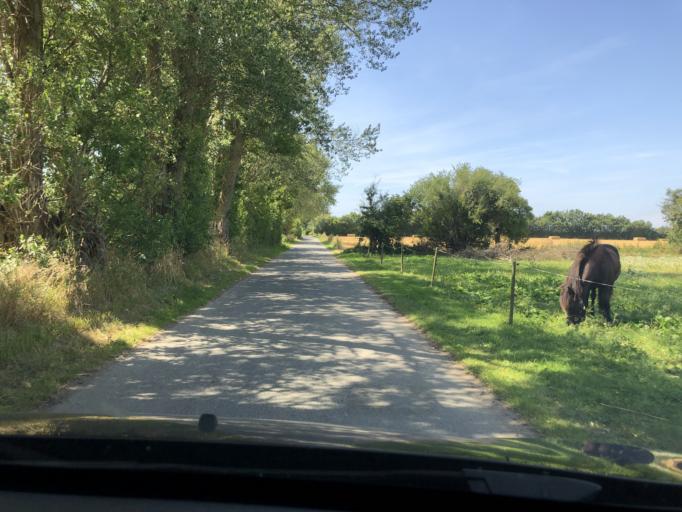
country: DK
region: South Denmark
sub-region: AEro Kommune
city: AEroskobing
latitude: 54.8931
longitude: 10.2969
